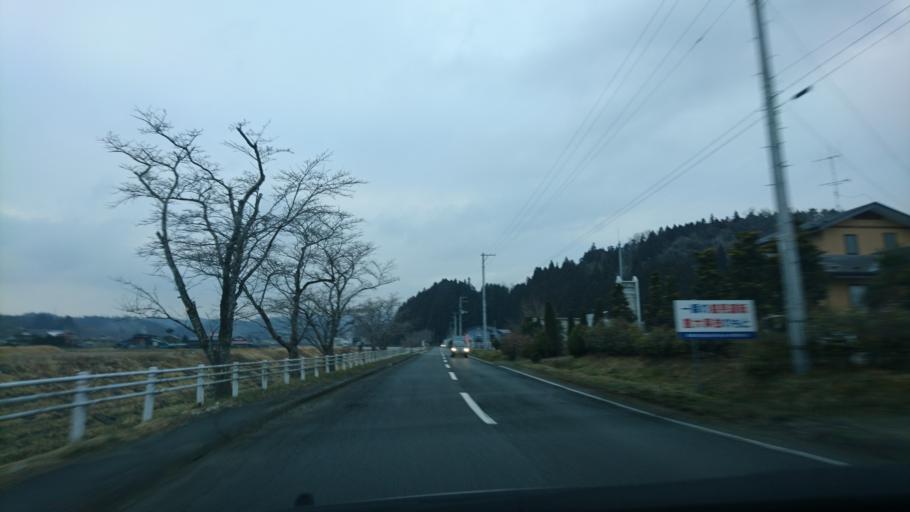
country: JP
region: Iwate
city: Ichinoseki
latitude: 39.0193
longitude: 141.3383
